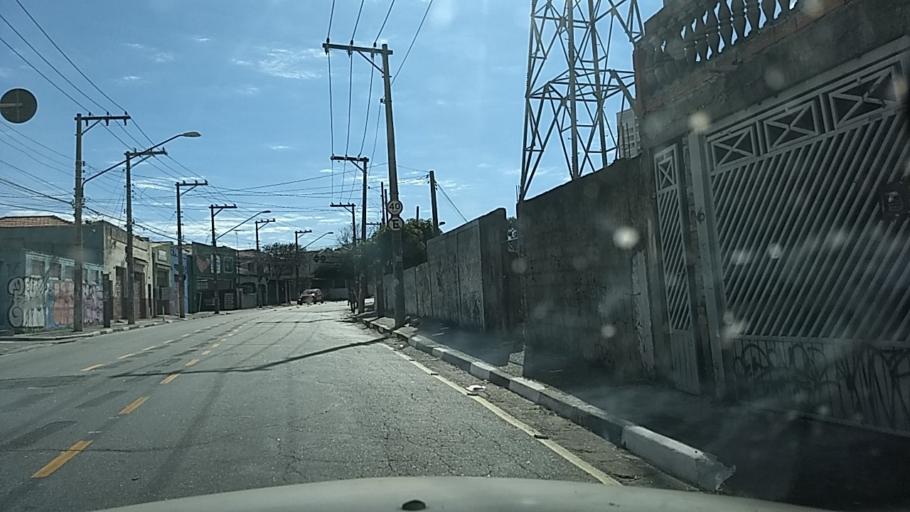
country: BR
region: Sao Paulo
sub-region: Sao Paulo
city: Sao Paulo
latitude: -23.4994
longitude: -46.5986
